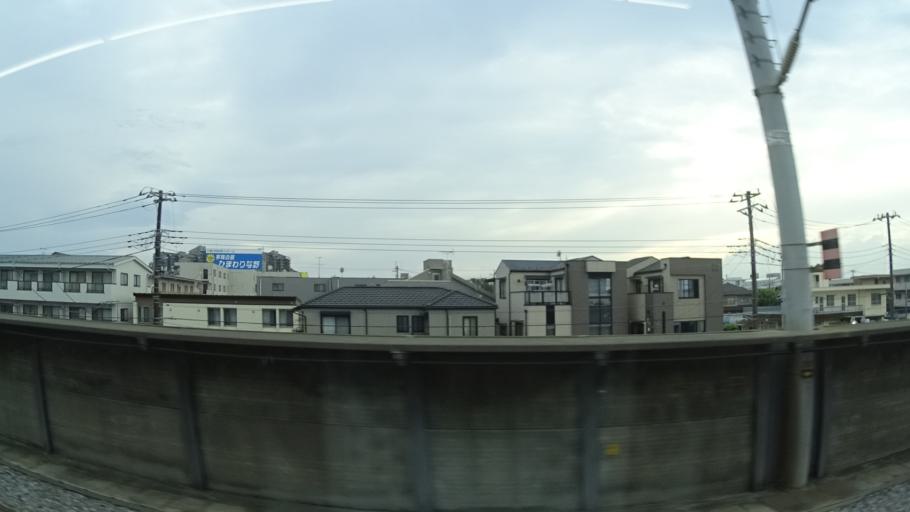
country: JP
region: Saitama
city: Yono
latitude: 35.8780
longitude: 139.6270
